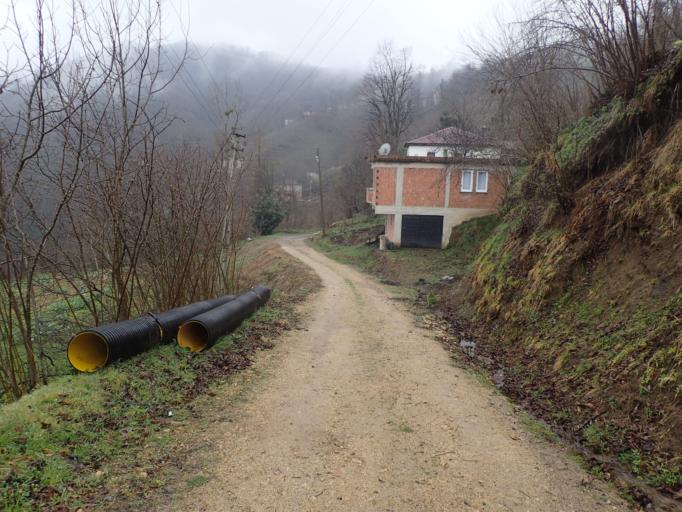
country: TR
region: Ordu
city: Camas
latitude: 40.9127
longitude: 37.5714
